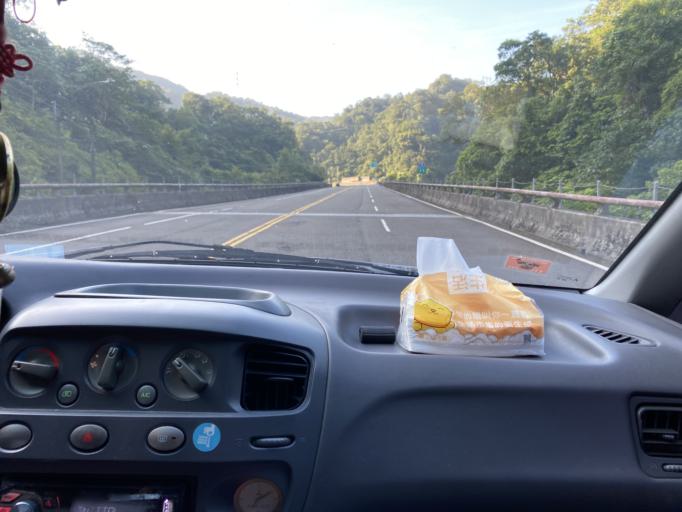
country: TW
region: Taiwan
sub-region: Keelung
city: Keelung
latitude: 25.0280
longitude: 121.7806
